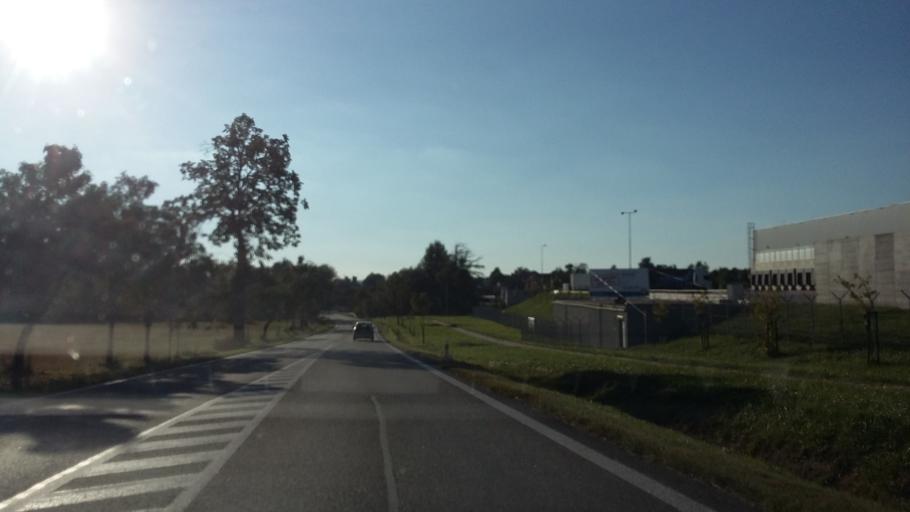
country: CZ
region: Vysocina
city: Merin
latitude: 49.3783
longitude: 15.9366
